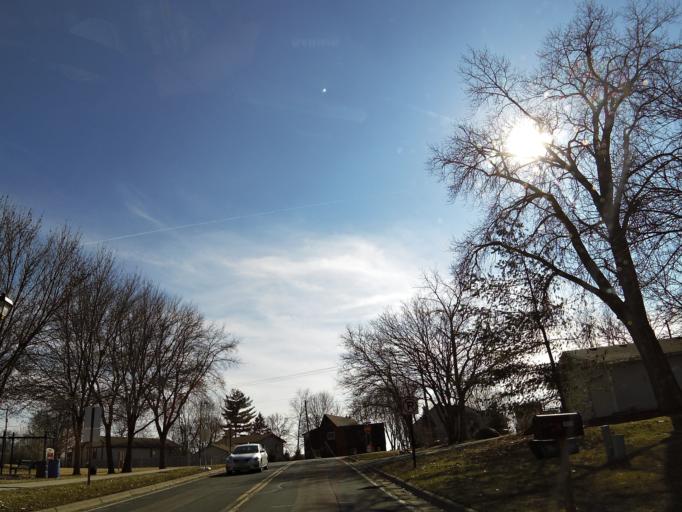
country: US
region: Minnesota
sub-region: Scott County
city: Prior Lake
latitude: 44.7069
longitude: -93.4633
